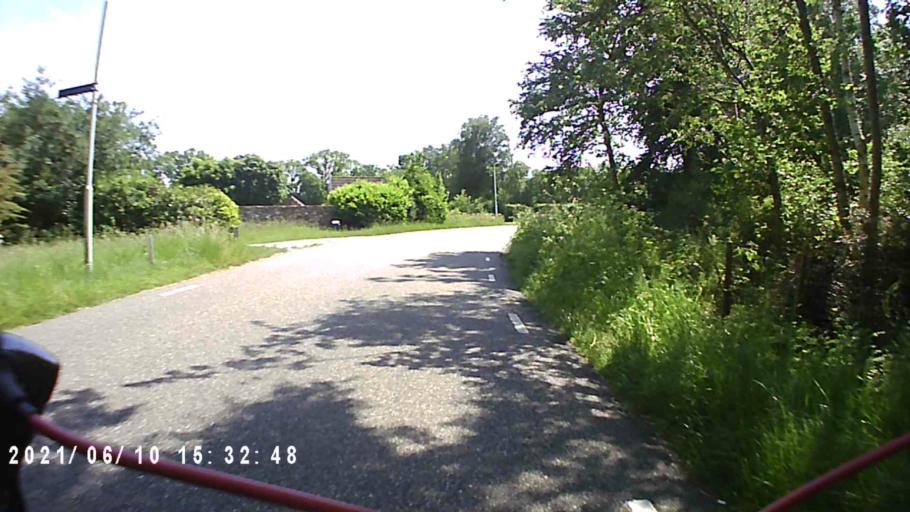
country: NL
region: Friesland
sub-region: Gemeente Achtkarspelen
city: Surhuisterveen
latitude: 53.1705
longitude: 6.1737
